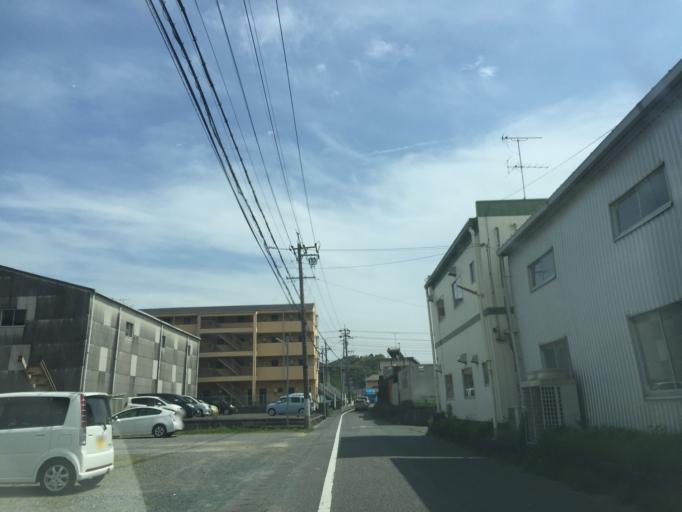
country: JP
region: Shizuoka
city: Kakegawa
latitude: 34.7805
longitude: 138.0336
